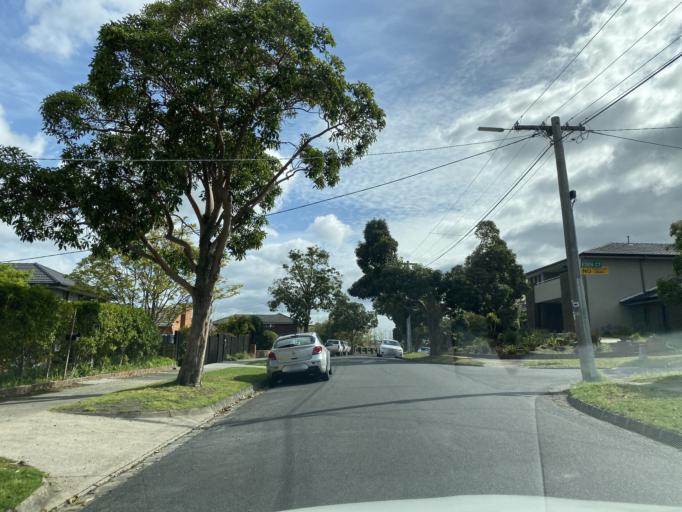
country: AU
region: Victoria
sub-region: Boroondara
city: Ashburton
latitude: -37.8487
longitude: 145.0913
